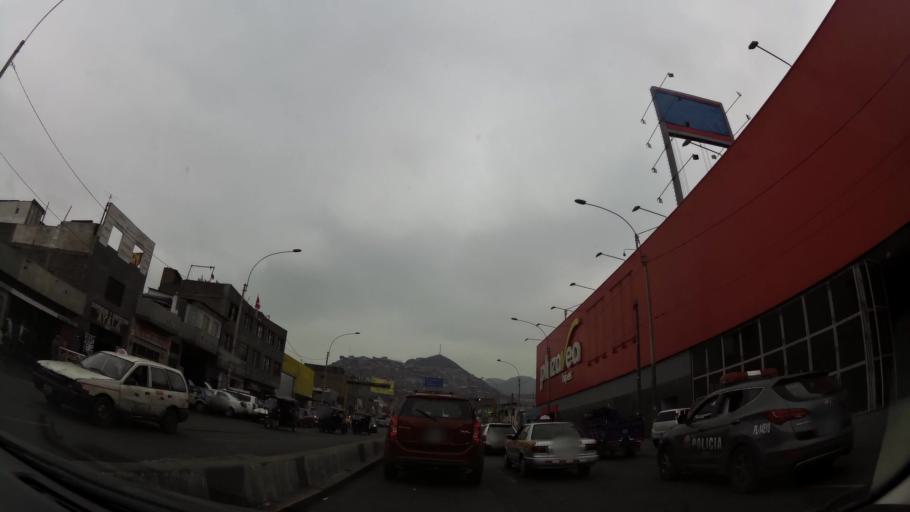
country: PE
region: Lima
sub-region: Lima
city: San Luis
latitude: -12.0654
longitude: -77.0048
